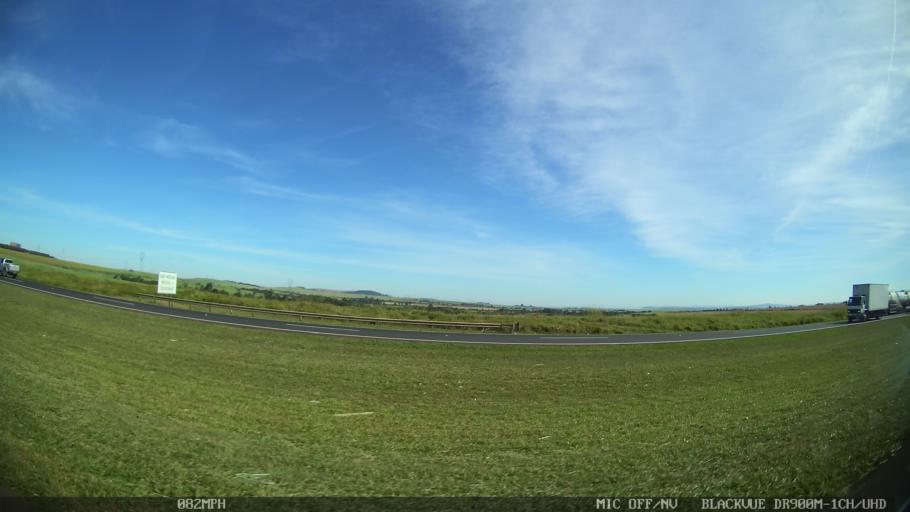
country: BR
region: Sao Paulo
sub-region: Araras
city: Araras
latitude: -22.4275
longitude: -47.3935
